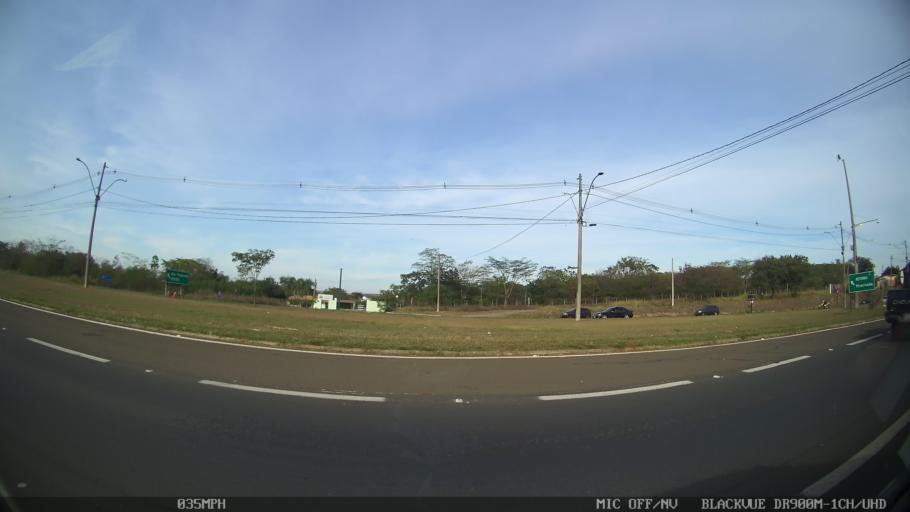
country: BR
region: Sao Paulo
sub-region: Piracicaba
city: Piracicaba
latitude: -22.6837
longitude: -47.6827
